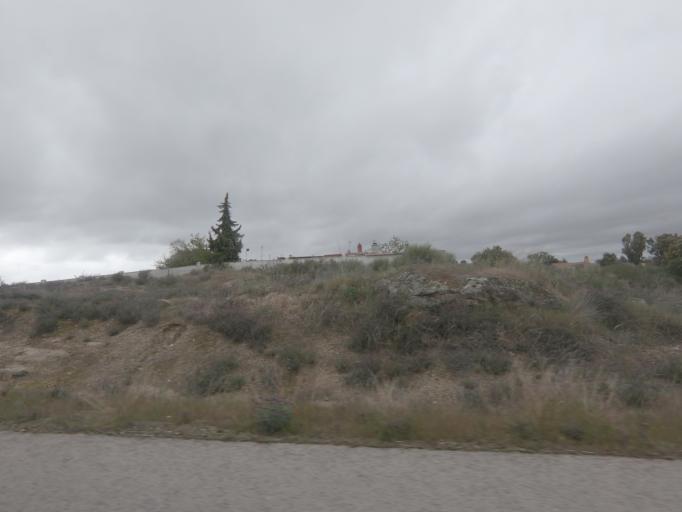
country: ES
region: Extremadura
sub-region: Provincia de Caceres
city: Malpartida de Caceres
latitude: 39.3824
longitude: -6.4437
